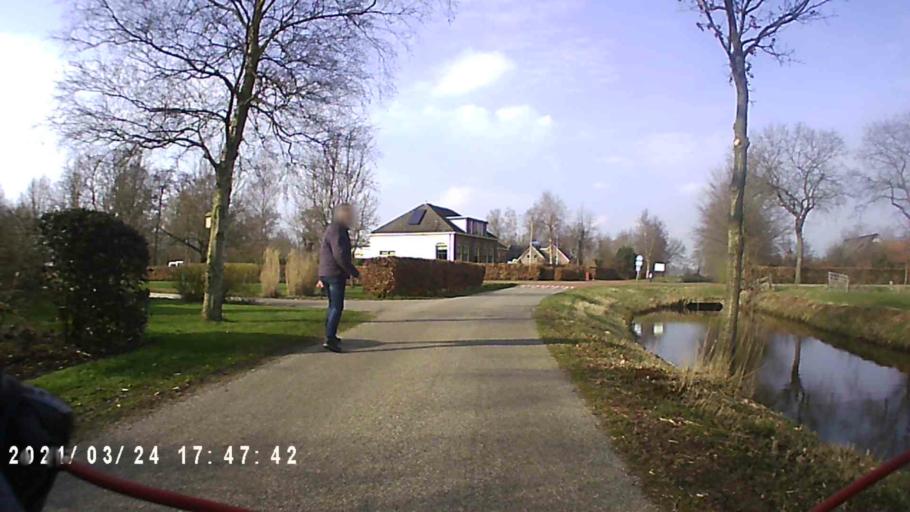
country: NL
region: Groningen
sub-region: Gemeente Leek
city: Leek
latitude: 53.1160
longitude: 6.3353
